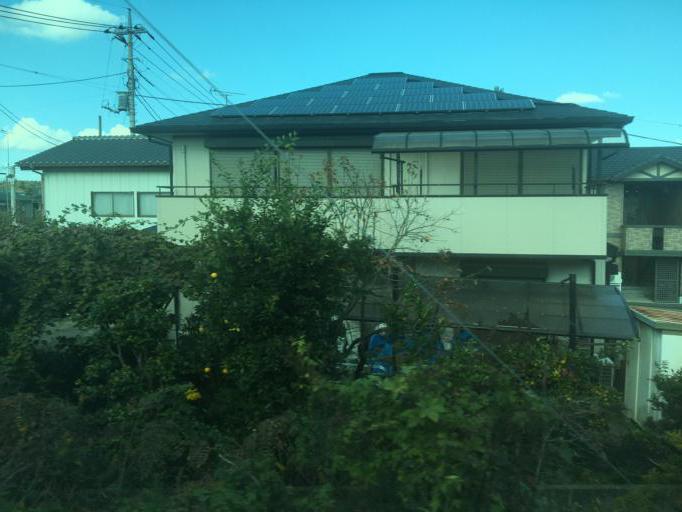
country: JP
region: Ibaraki
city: Tomobe
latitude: 36.3445
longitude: 140.2899
